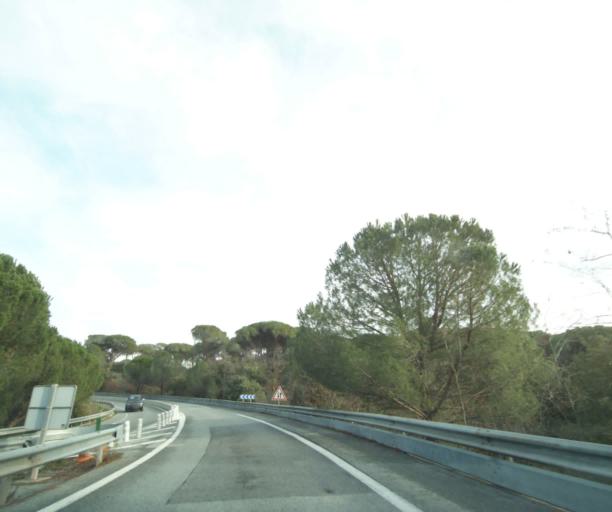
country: FR
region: Provence-Alpes-Cote d'Azur
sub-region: Departement du Var
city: Le Muy
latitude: 43.4573
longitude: 6.5518
